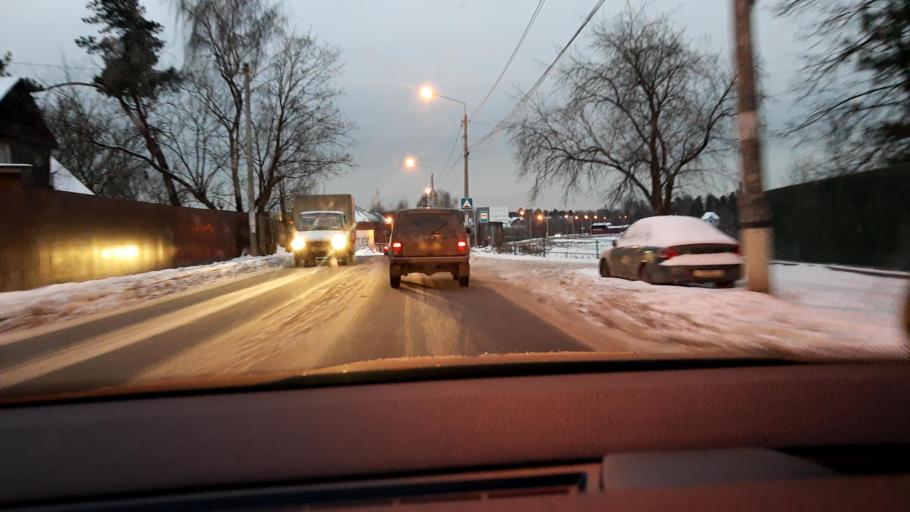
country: RU
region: Moskovskaya
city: Tomilino
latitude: 55.6482
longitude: 37.9556
